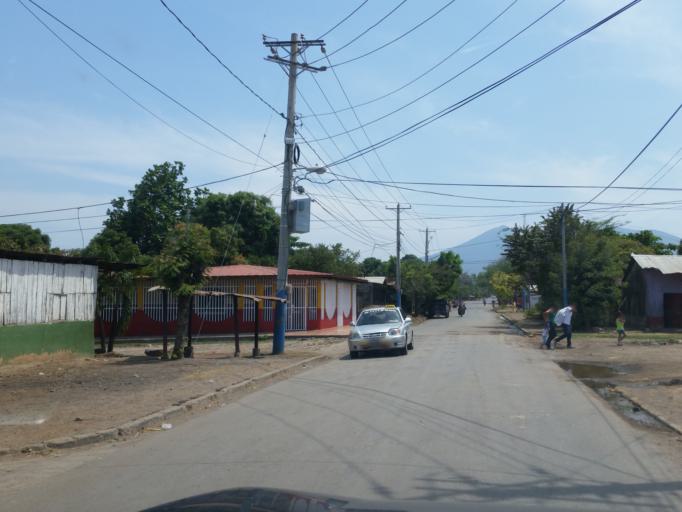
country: NI
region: Granada
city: Granada
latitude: 11.9453
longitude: -85.9622
